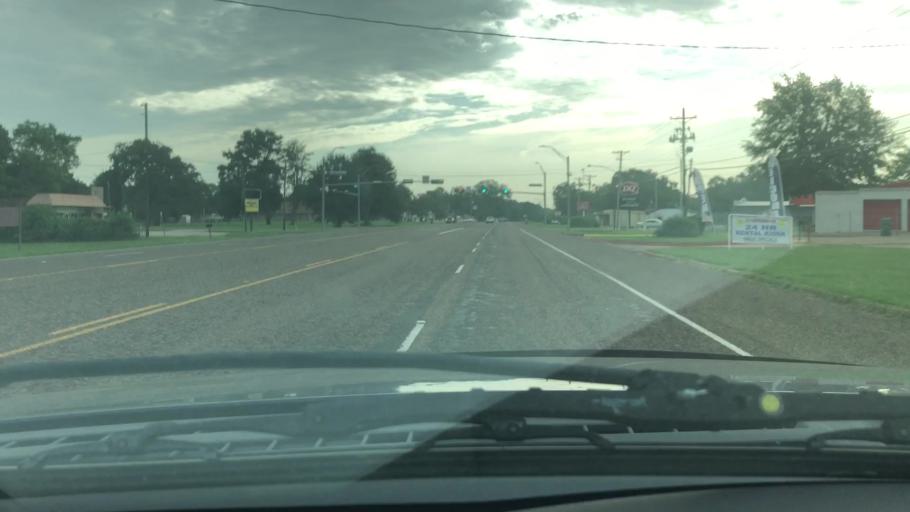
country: US
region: Texas
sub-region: Bowie County
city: Wake Village
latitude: 33.4009
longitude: -94.0817
